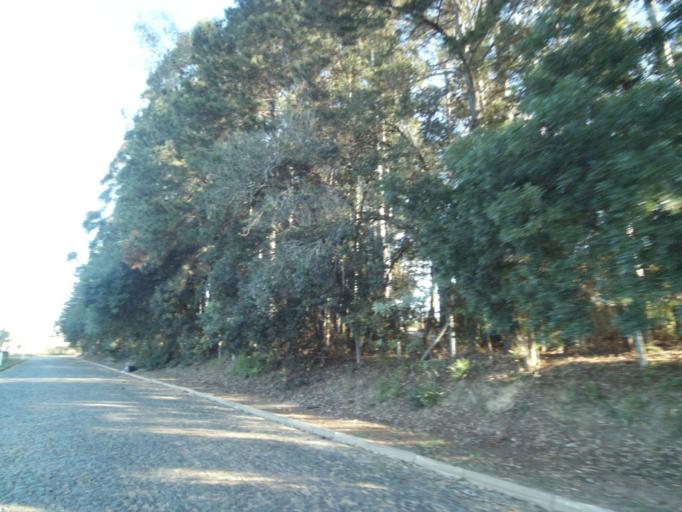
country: BR
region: Parana
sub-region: Tibagi
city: Tibagi
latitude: -24.5068
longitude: -50.4171
